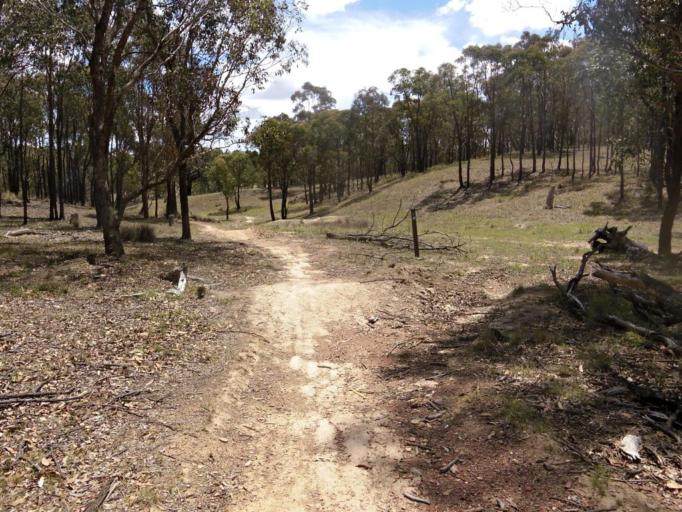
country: AU
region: Australian Capital Territory
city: Kaleen
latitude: -35.1369
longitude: 149.1460
